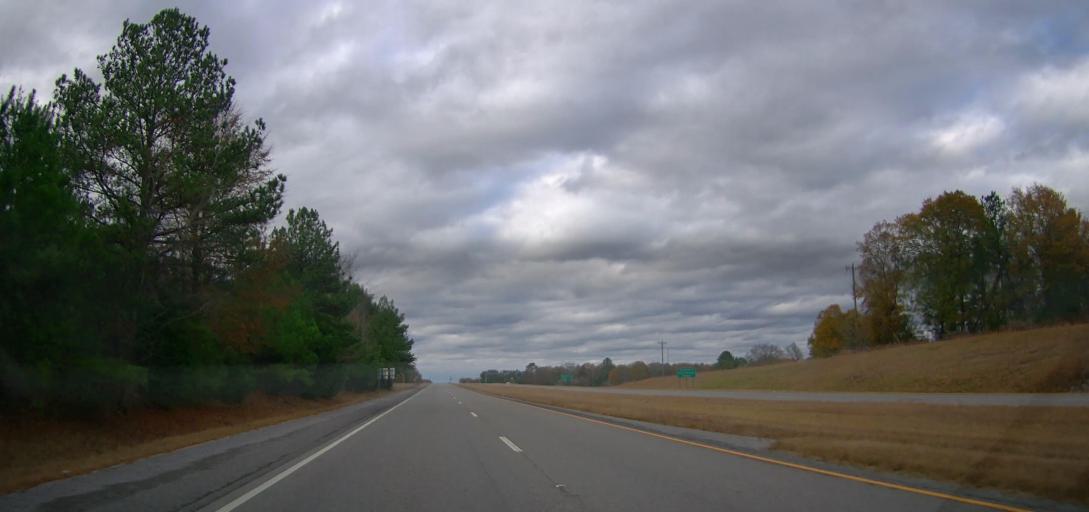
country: US
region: Alabama
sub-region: Lawrence County
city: Moulton
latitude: 34.5174
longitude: -87.2931
